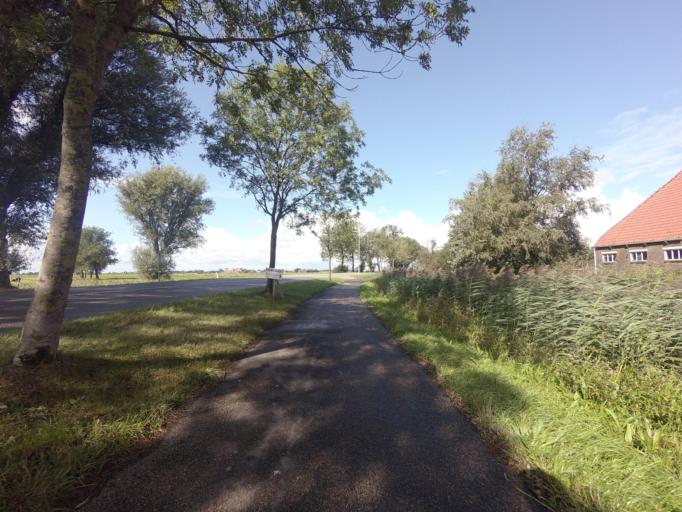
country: NL
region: Friesland
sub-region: Gemeente Boarnsterhim
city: Warten
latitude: 53.1503
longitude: 5.8772
